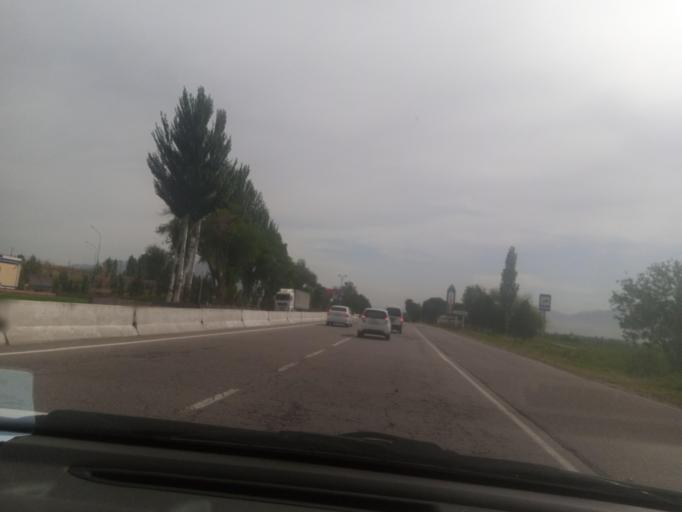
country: UZ
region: Toshkent
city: Angren
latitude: 40.9724
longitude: 69.9935
